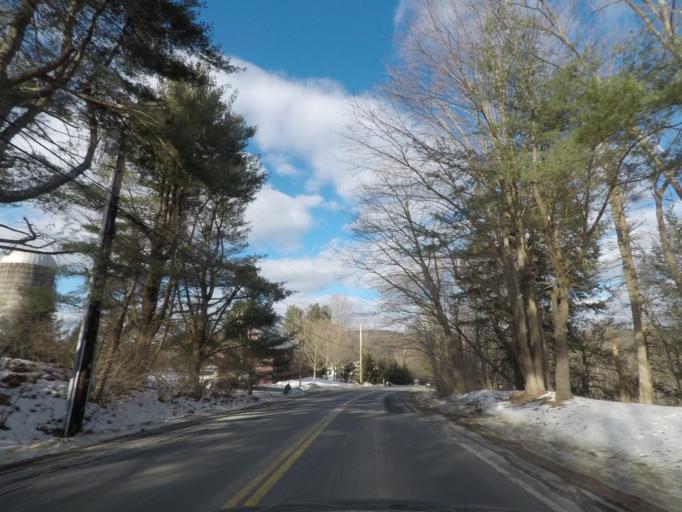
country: US
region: Massachusetts
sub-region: Berkshire County
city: Richmond
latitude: 42.4652
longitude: -73.4238
